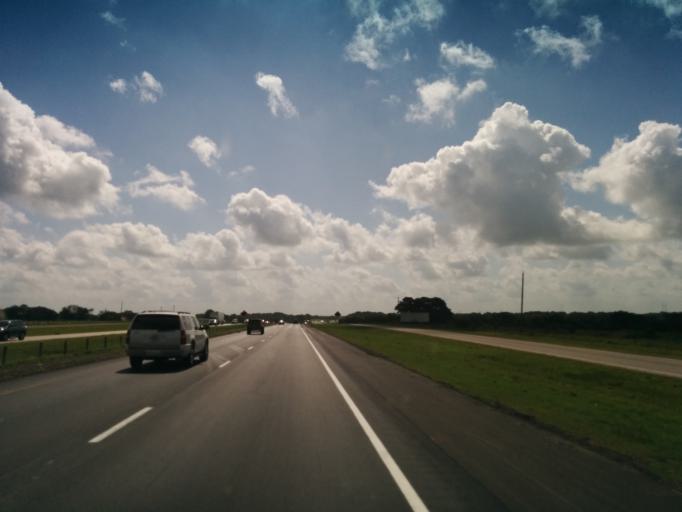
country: US
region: Texas
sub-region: Colorado County
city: Weimar
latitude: 29.6922
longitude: -96.7400
